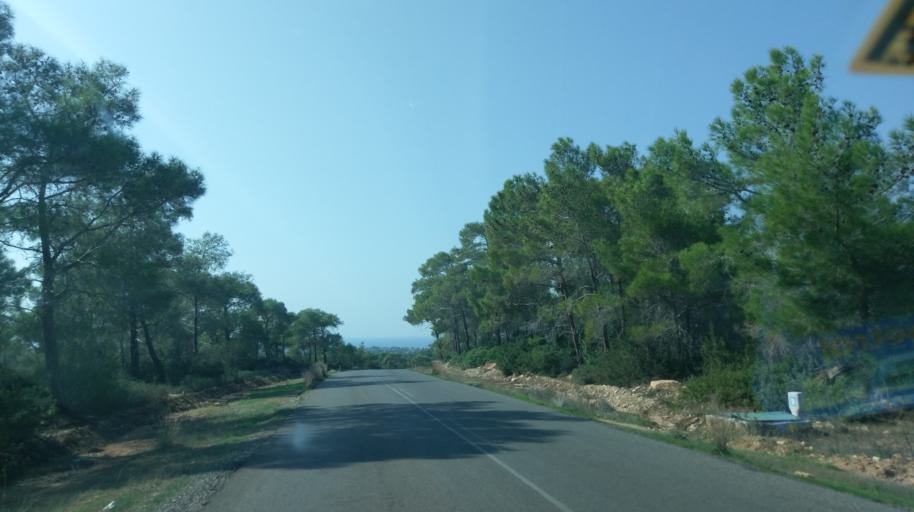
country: CY
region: Lefkosia
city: Morfou
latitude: 35.3021
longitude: 32.9961
